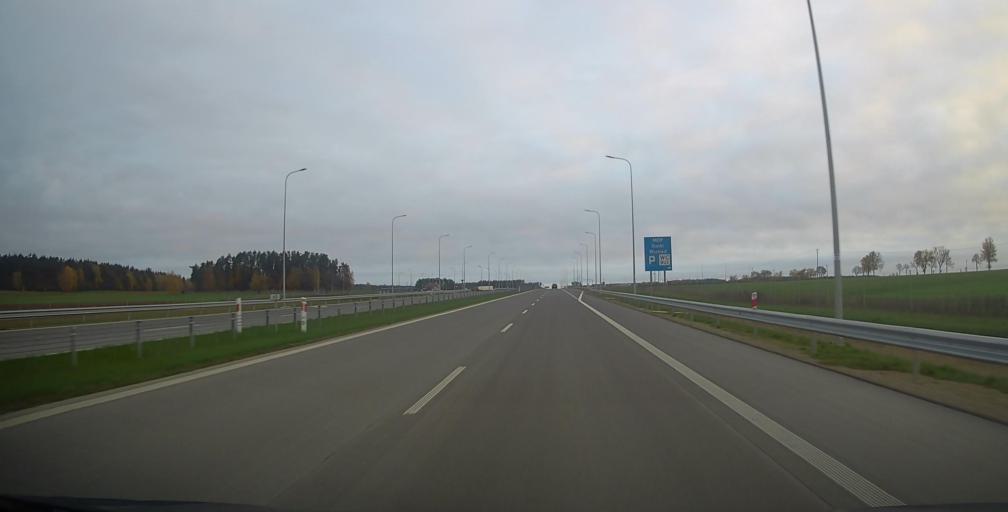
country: PL
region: Podlasie
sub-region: Powiat lomzynski
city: Piatnica
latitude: 53.2665
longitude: 22.1224
